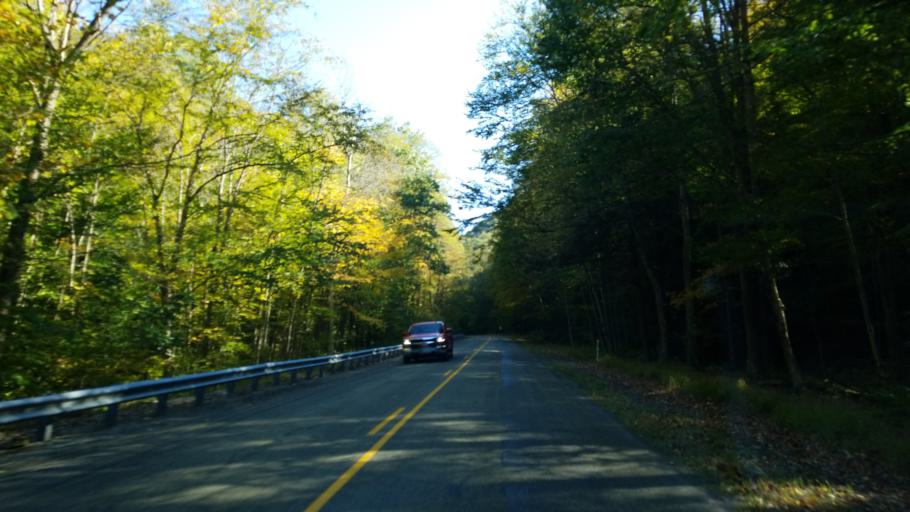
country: US
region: Pennsylvania
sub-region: Clearfield County
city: Shiloh
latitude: 41.2566
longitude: -78.3866
